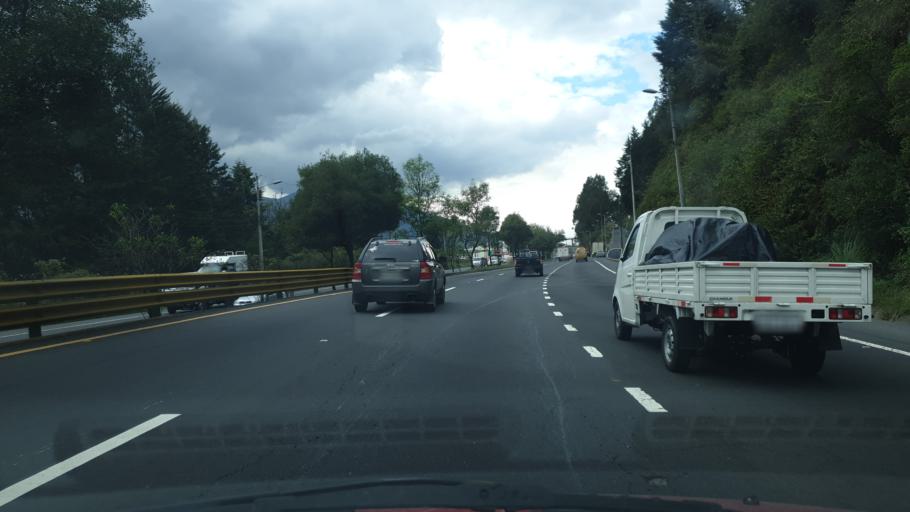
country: EC
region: Pichincha
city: Quito
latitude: -0.2457
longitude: -78.4817
